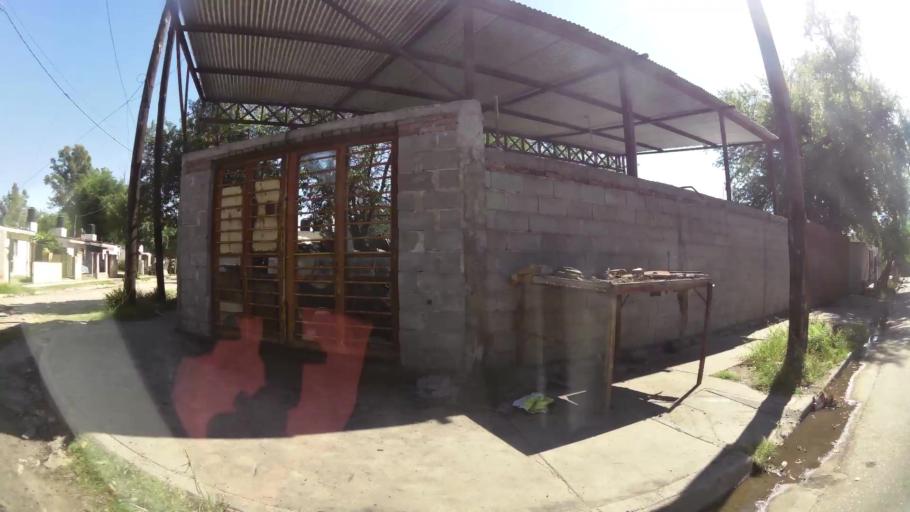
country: AR
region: Cordoba
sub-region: Departamento de Capital
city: Cordoba
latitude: -31.4411
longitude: -64.1311
